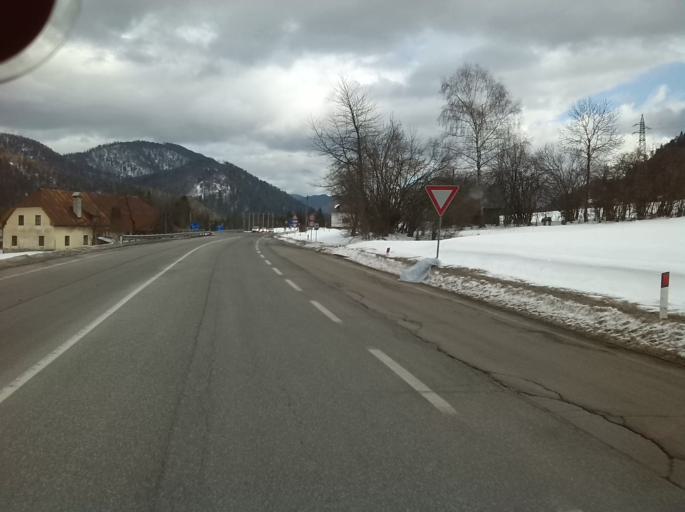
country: IT
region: Friuli Venezia Giulia
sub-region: Provincia di Udine
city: Tarvisio
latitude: 46.5076
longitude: 13.5399
